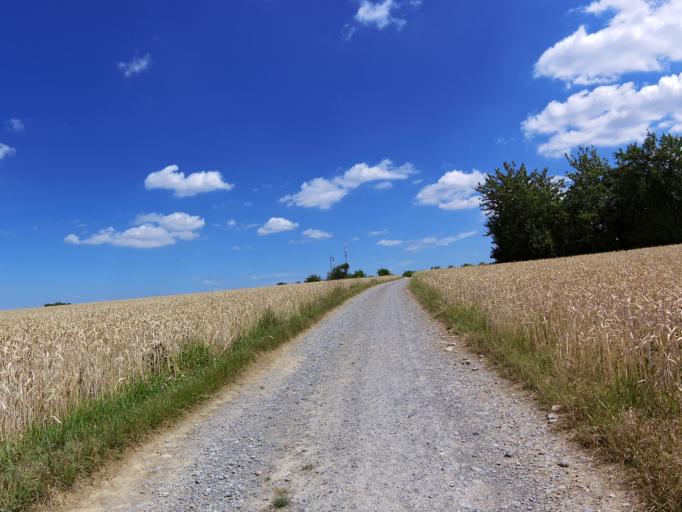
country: DE
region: Bavaria
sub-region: Regierungsbezirk Unterfranken
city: Hochberg
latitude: 49.7802
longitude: 9.8863
